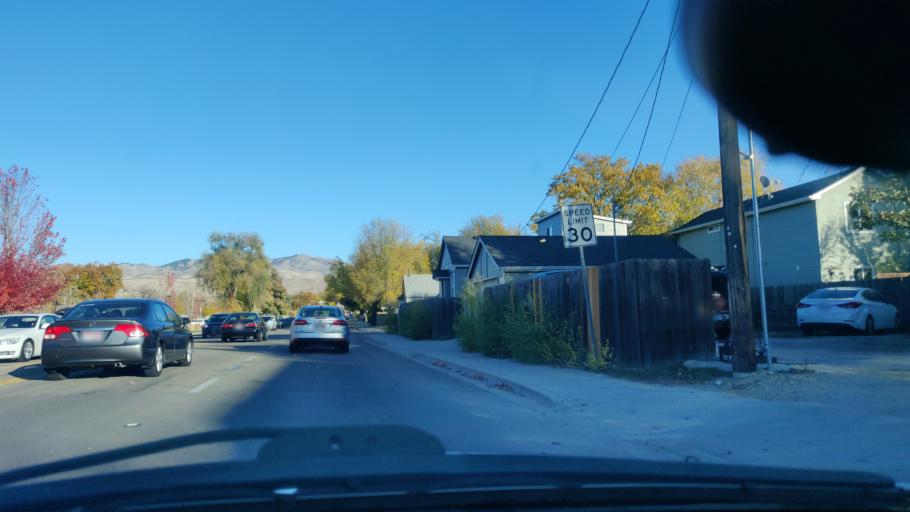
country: US
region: Idaho
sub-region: Ada County
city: Boise
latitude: 43.5983
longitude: -116.2019
